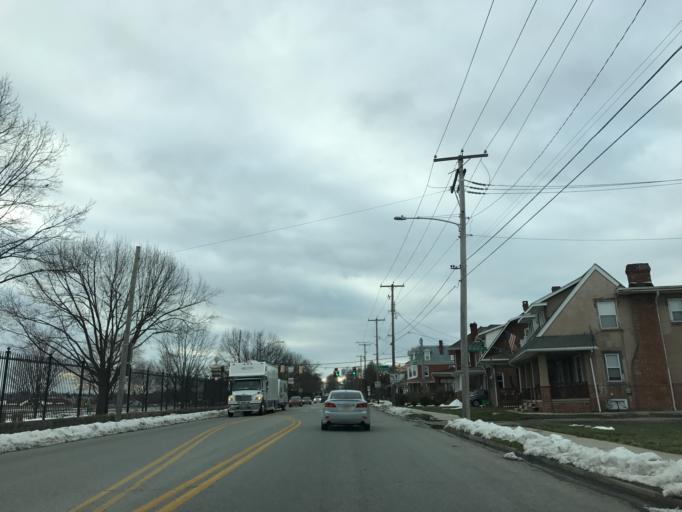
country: US
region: Pennsylvania
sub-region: York County
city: West York
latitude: 39.9591
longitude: -76.7526
